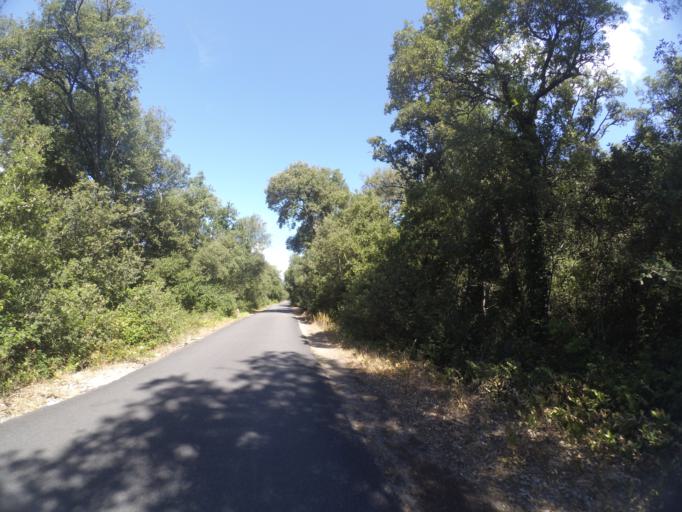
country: FR
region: Poitou-Charentes
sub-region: Departement de la Charente-Maritime
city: Les Mathes
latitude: 45.6722
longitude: -1.1486
